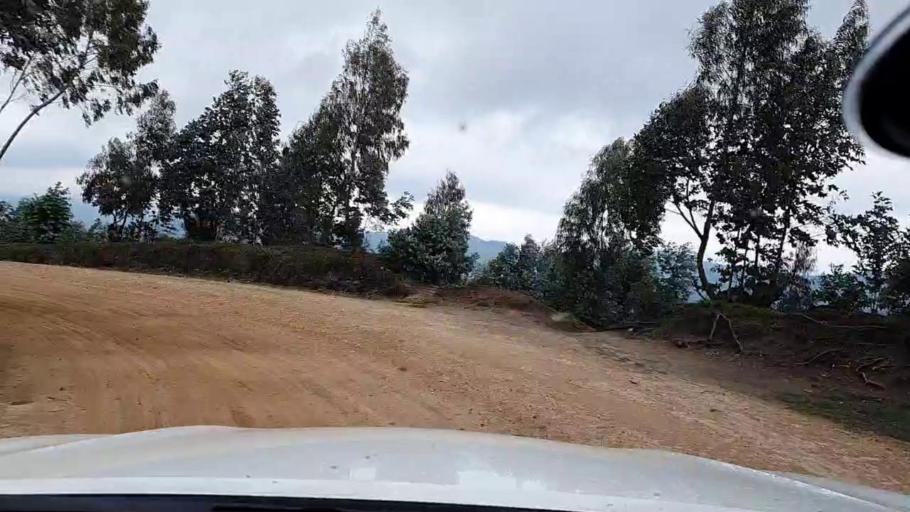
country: RW
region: Western Province
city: Kibuye
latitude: -2.2476
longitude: 29.3434
